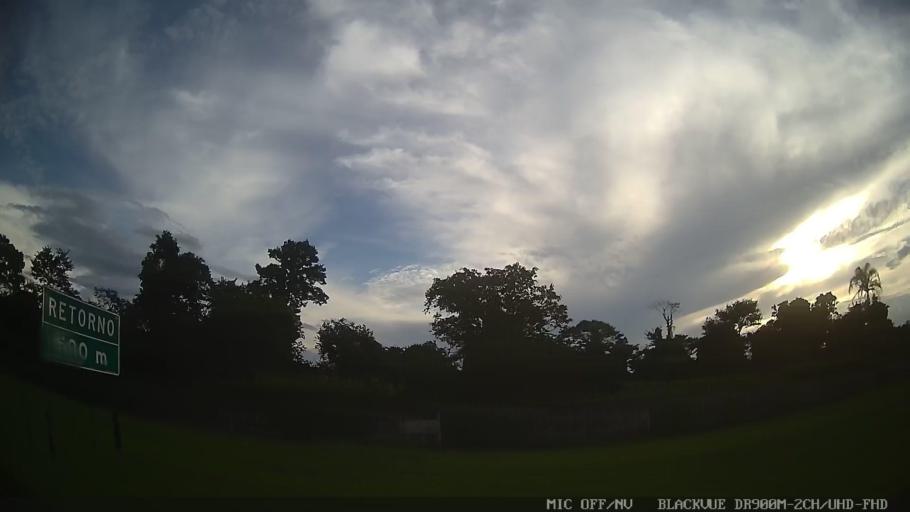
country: BR
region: Sao Paulo
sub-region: Porto Feliz
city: Porto Feliz
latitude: -23.2110
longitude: -47.5800
